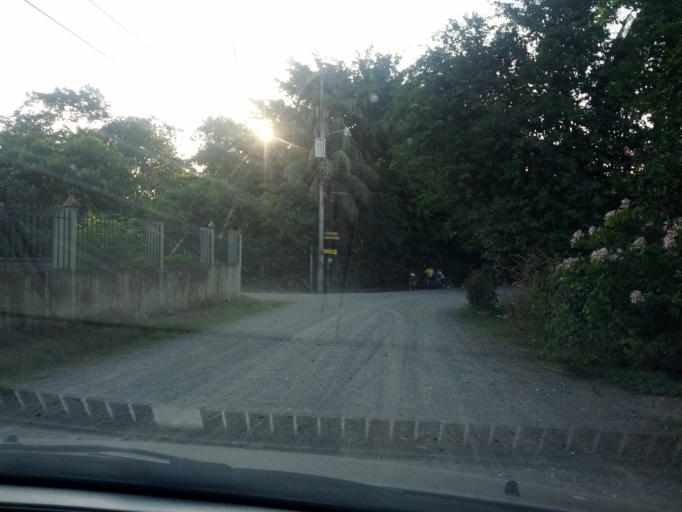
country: CR
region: Puntarenas
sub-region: Canton de Golfito
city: Golfito
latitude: 8.5355
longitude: -83.3019
